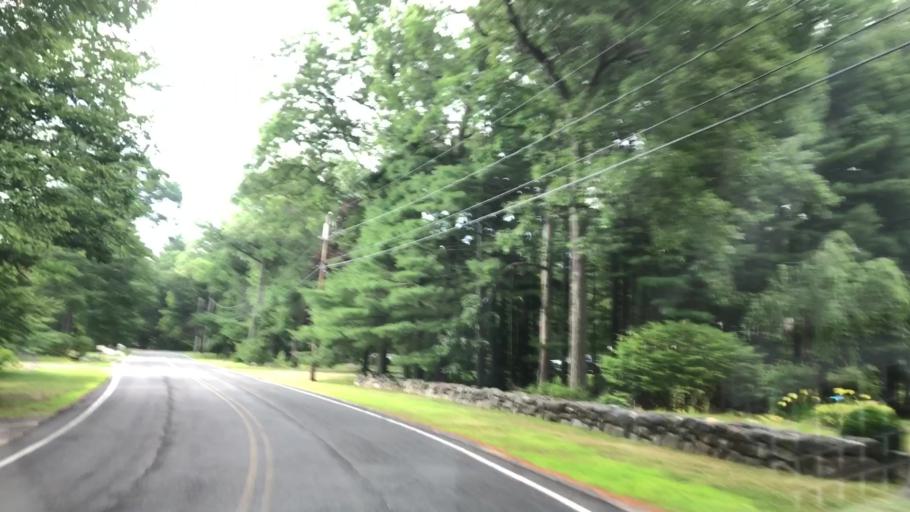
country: US
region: Massachusetts
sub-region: Hampshire County
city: Southampton
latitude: 42.2157
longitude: -72.7452
